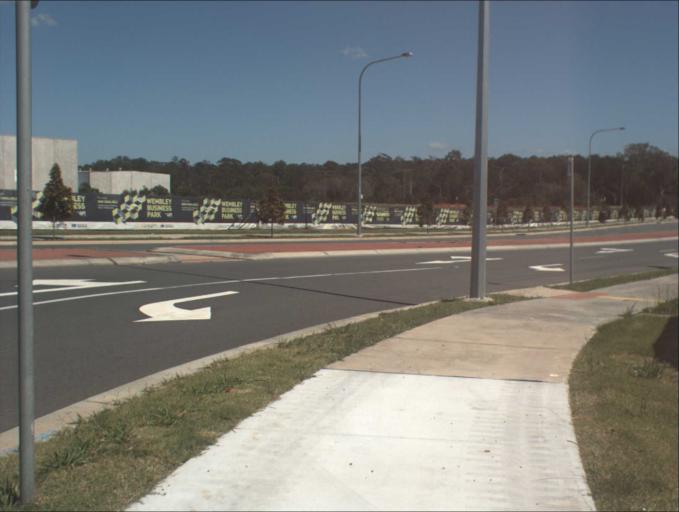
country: AU
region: Queensland
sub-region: Logan
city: Woodridge
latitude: -27.6474
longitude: 153.0955
